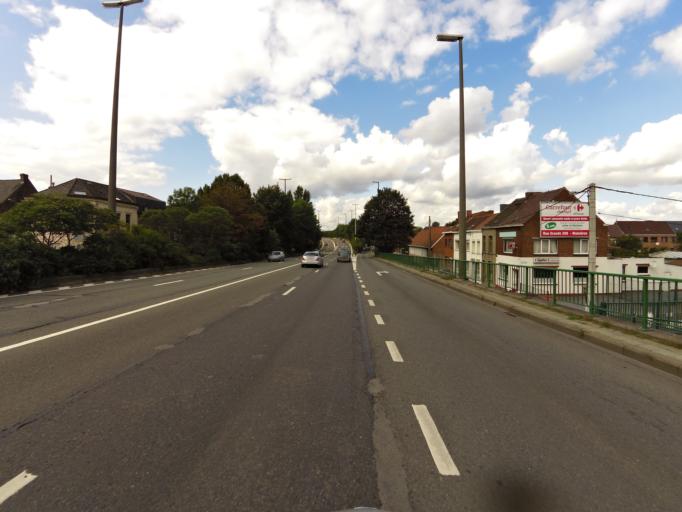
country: BE
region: Wallonia
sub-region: Province du Hainaut
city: Mons
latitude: 50.4608
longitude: 3.9451
